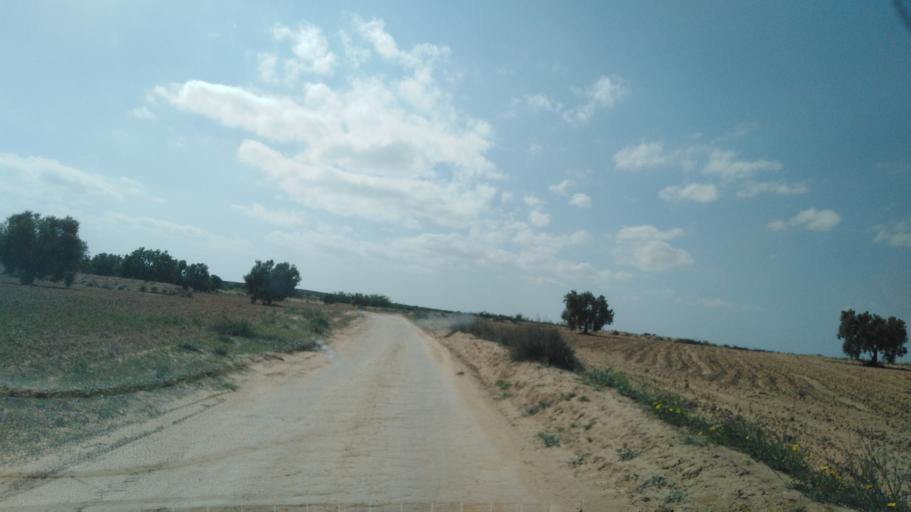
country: TN
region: Safaqis
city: Bi'r `Ali Bin Khalifah
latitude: 34.8002
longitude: 10.3813
